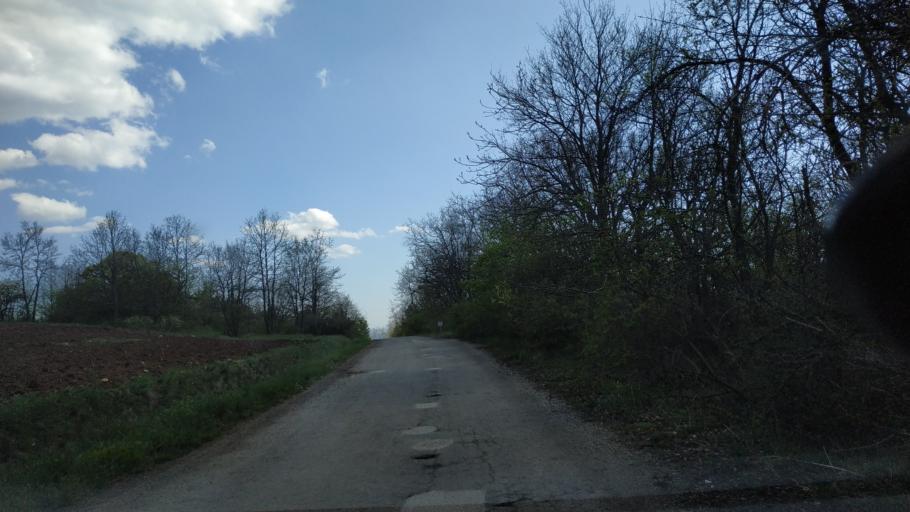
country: RS
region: Central Serbia
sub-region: Zajecarski Okrug
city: Soko Banja
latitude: 43.5564
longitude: 21.8930
